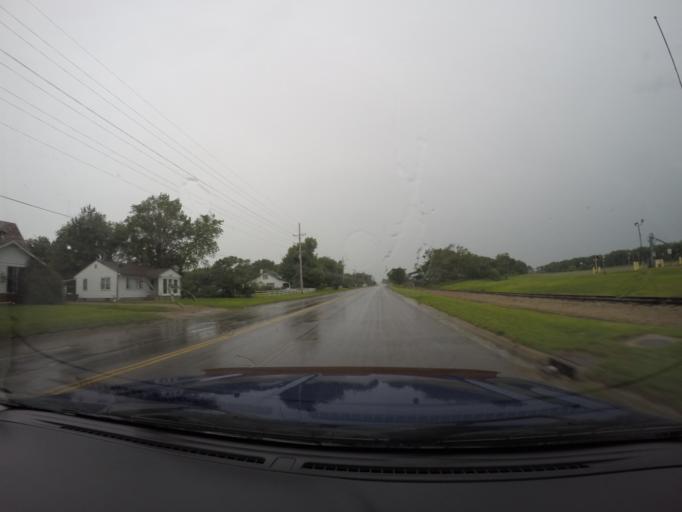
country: US
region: Kansas
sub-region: Cloud County
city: Concordia
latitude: 39.5736
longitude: -97.6795
